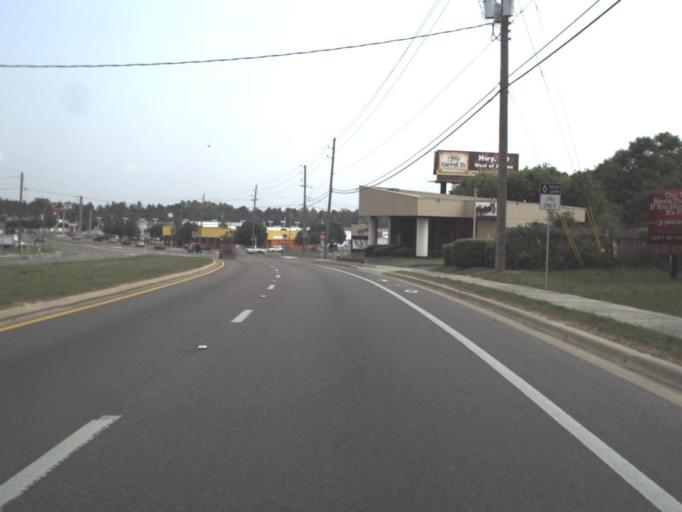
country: US
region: Florida
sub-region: Santa Rosa County
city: Milton
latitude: 30.6192
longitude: -87.0552
